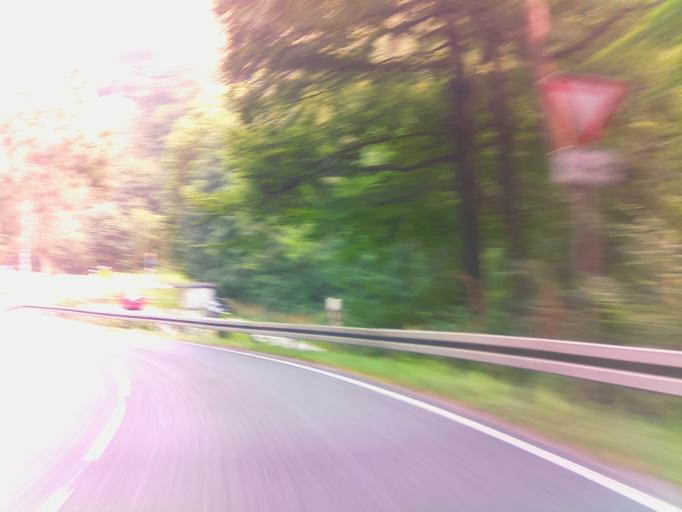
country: DE
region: Thuringia
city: Troistedt
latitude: 50.9179
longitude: 11.2548
